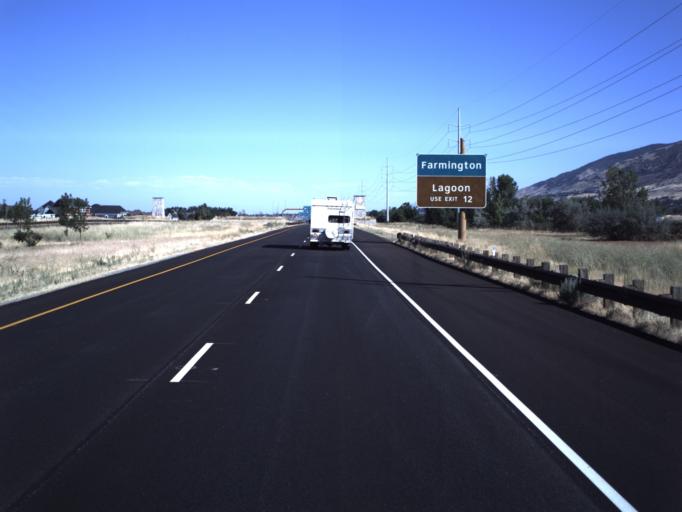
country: US
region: Utah
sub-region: Davis County
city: Farmington
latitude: 40.9670
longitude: -111.8932
